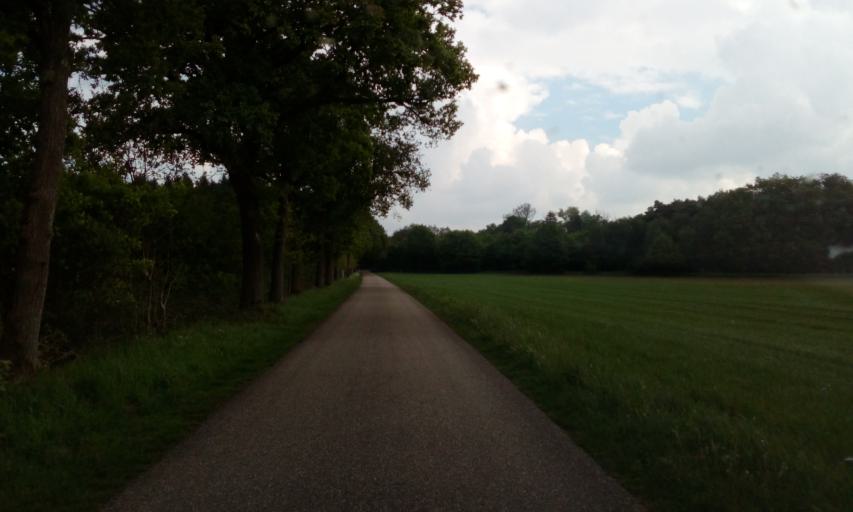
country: NL
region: Gelderland
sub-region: Gemeente Voorst
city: Voorst
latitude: 52.1857
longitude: 6.1466
